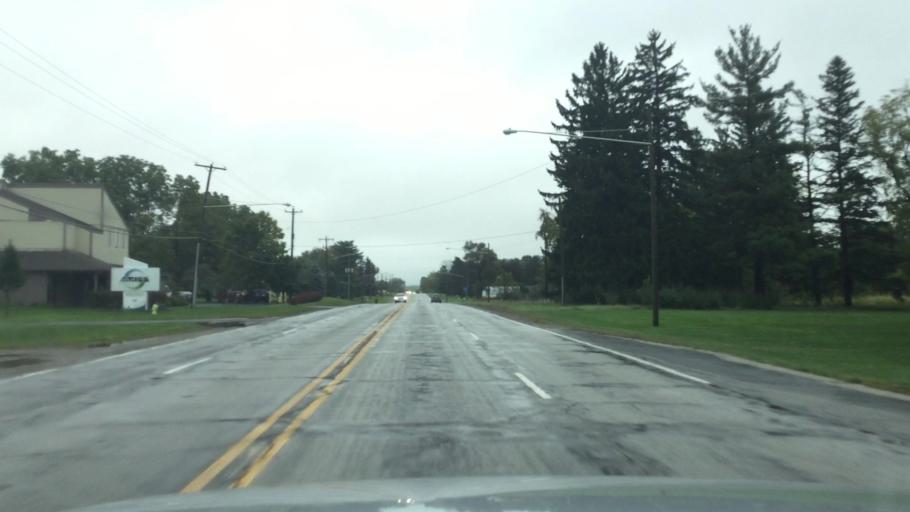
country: US
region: Michigan
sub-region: Saginaw County
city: Bridgeport
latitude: 43.3451
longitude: -83.8534
